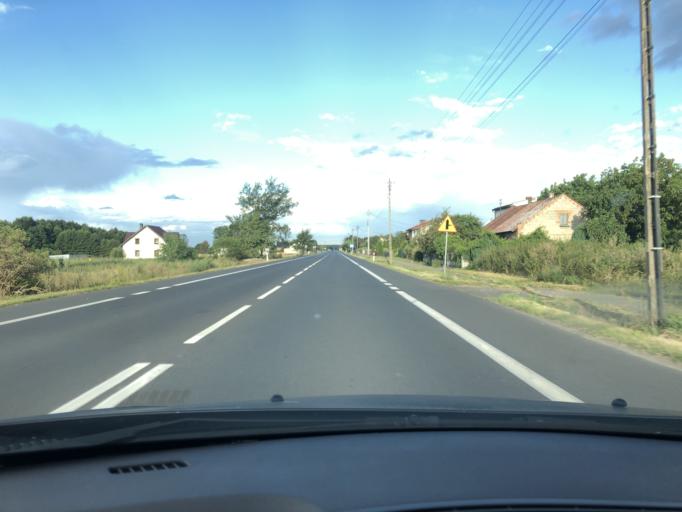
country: PL
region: Lodz Voivodeship
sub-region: Powiat wieruszowski
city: Galewice
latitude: 51.3036
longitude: 18.2665
